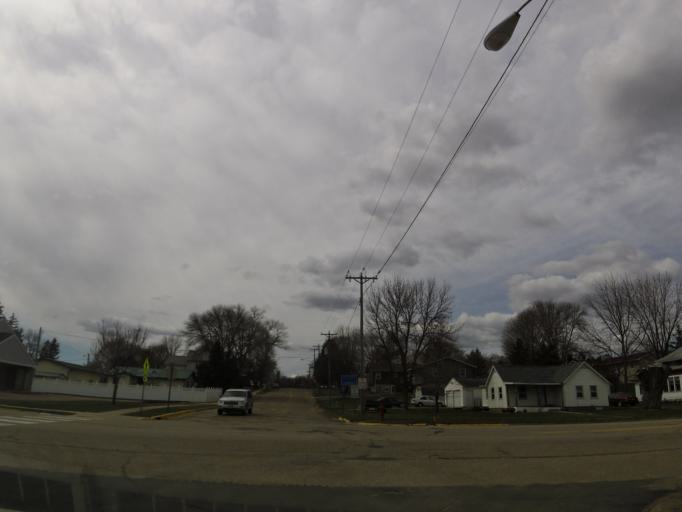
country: US
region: Minnesota
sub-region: Goodhue County
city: Pine Island
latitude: 44.1983
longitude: -92.6462
